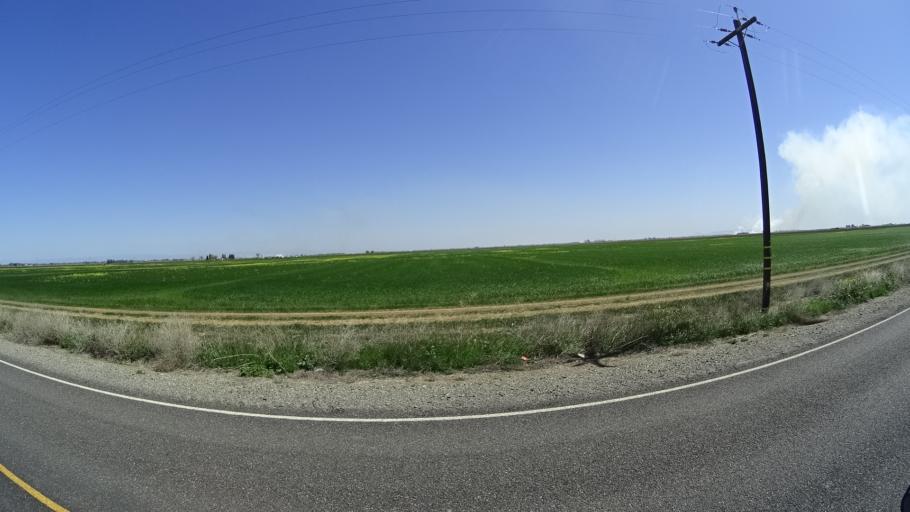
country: US
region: California
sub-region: Glenn County
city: Willows
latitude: 39.4820
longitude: -122.2490
